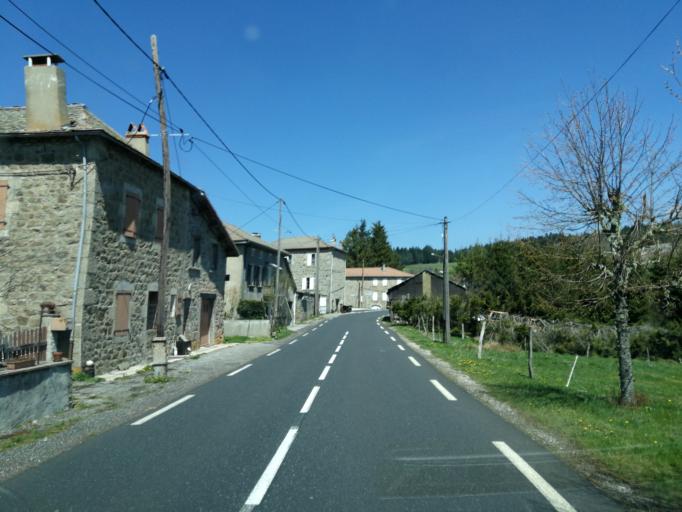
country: FR
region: Rhone-Alpes
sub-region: Departement de l'Ardeche
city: Saint-Agreve
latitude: 45.1203
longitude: 4.4093
